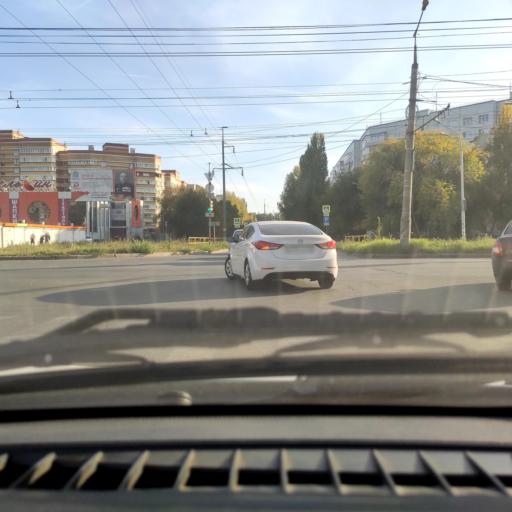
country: RU
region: Samara
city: Tol'yatti
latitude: 53.5115
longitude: 49.4425
